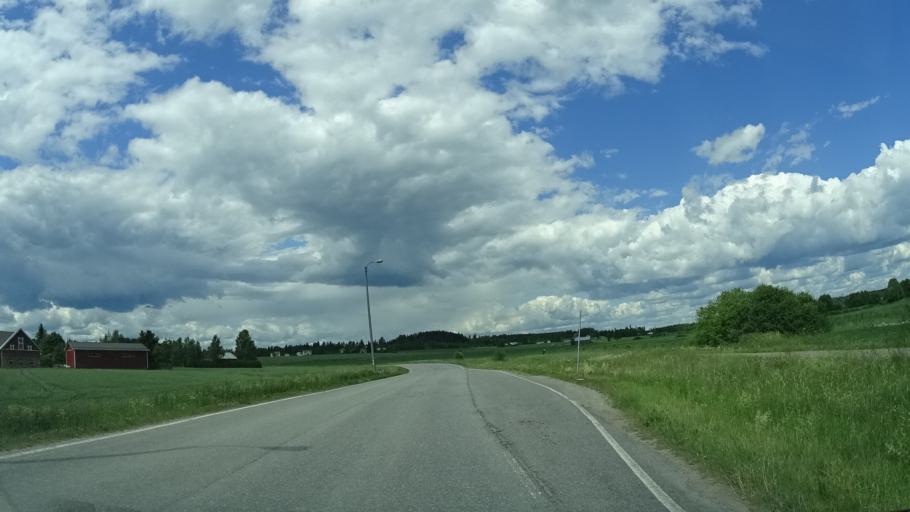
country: FI
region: Uusimaa
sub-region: Helsinki
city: Nurmijaervi
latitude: 60.4005
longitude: 24.6355
